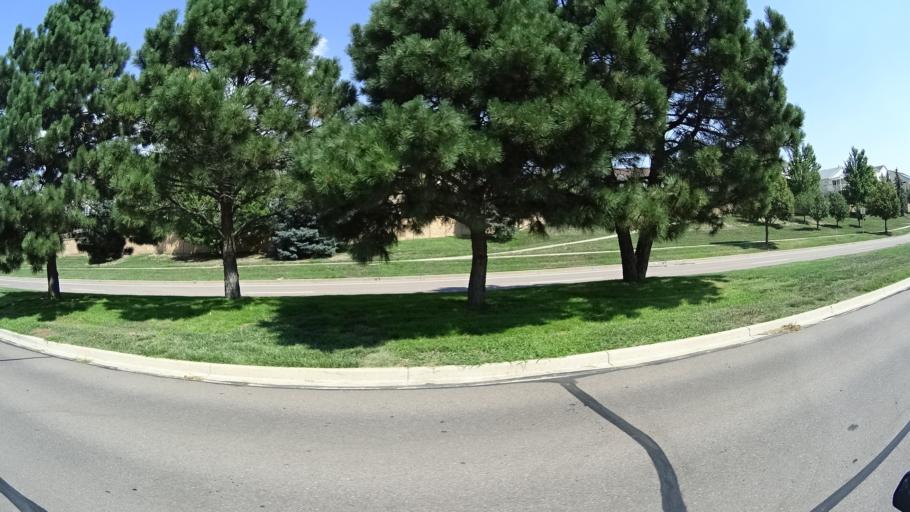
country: US
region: Colorado
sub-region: El Paso County
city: Cimarron Hills
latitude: 38.9290
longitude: -104.7324
